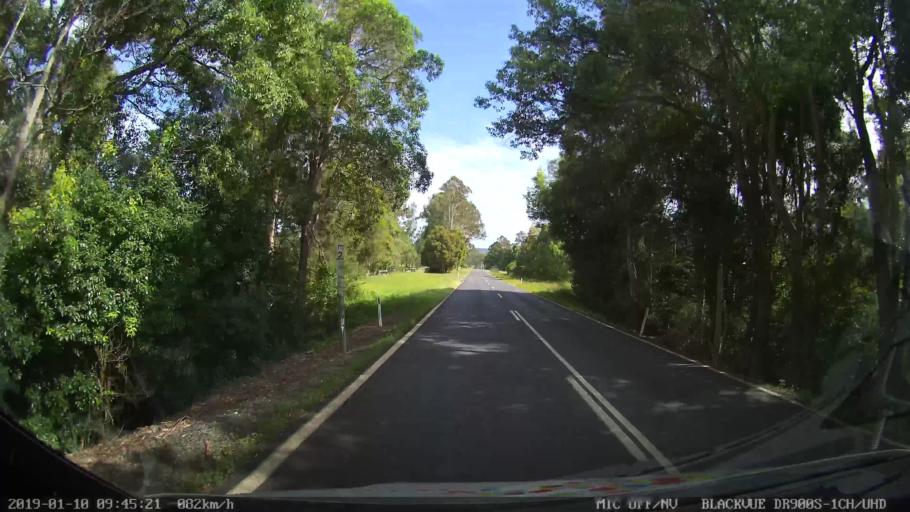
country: AU
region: New South Wales
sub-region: Coffs Harbour
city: Nana Glen
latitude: -30.1056
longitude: 153.0040
